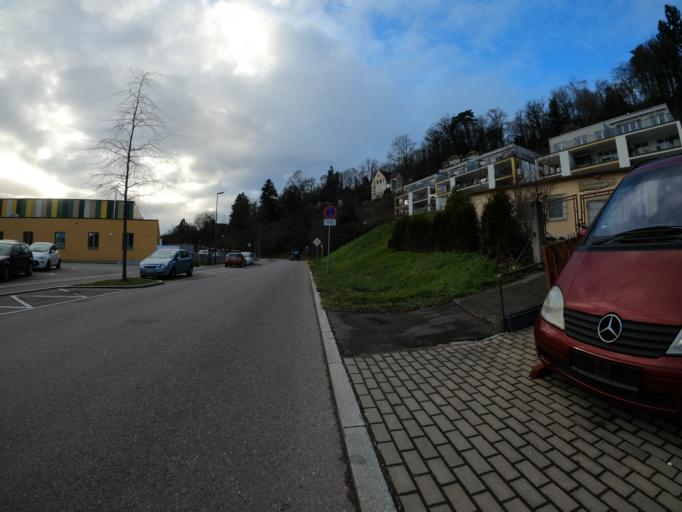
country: DE
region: Baden-Wuerttemberg
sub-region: Regierungsbezirk Stuttgart
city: Schwabisch Gmund
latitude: 48.8006
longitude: 9.7843
